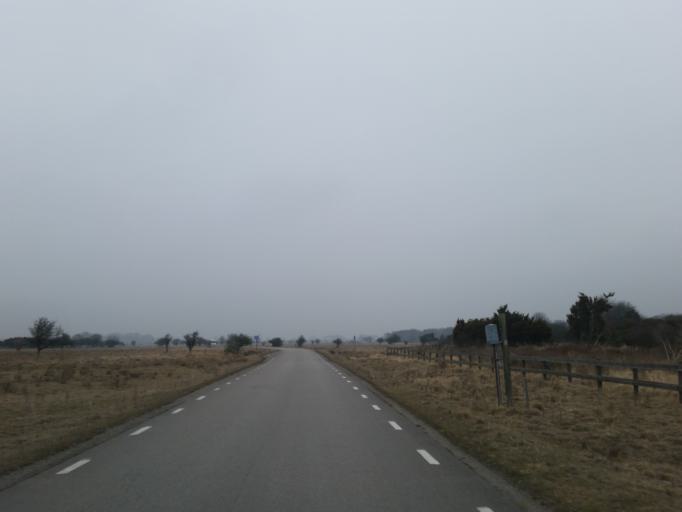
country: SE
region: Kalmar
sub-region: Morbylanga Kommun
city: Moerbylanga
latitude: 56.2184
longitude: 16.4097
